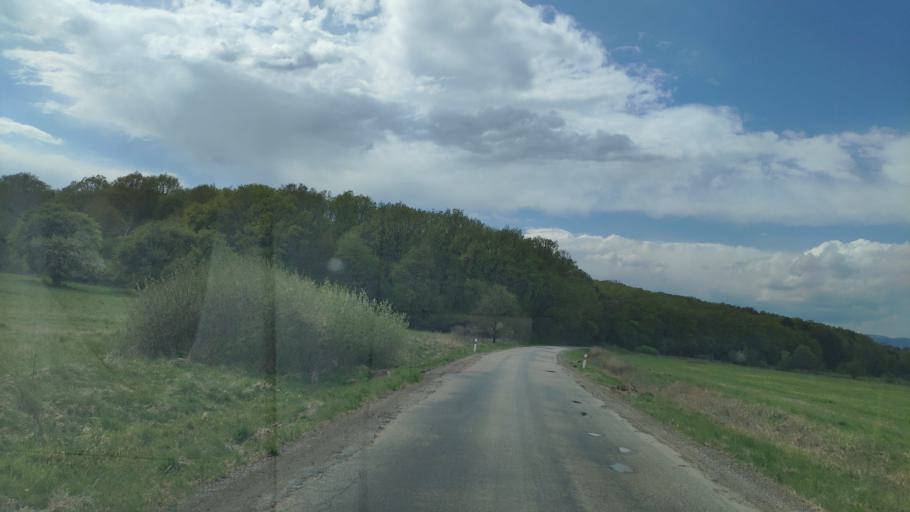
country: SK
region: Kosicky
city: Moldava nad Bodvou
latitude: 48.5688
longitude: 20.9368
